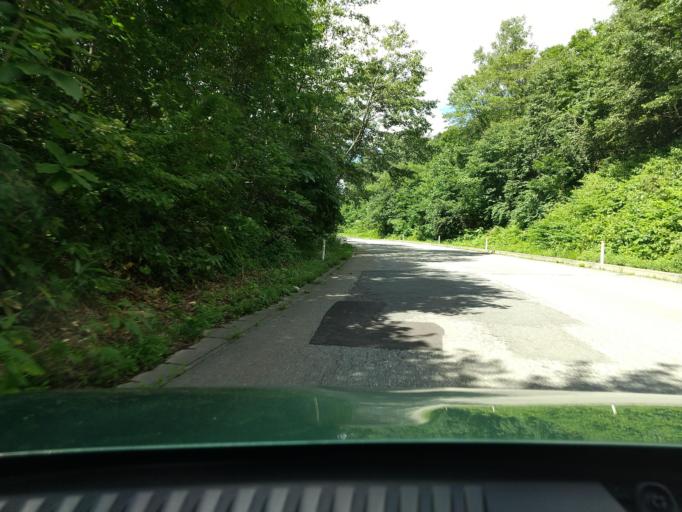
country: JP
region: Iwate
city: Shizukuishi
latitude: 39.7747
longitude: 140.7640
